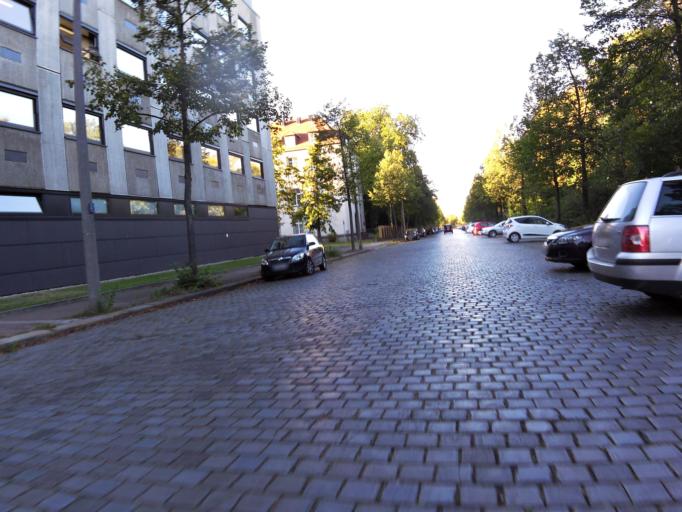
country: DE
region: Saxony
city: Leipzig
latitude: 51.3275
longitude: 12.3929
